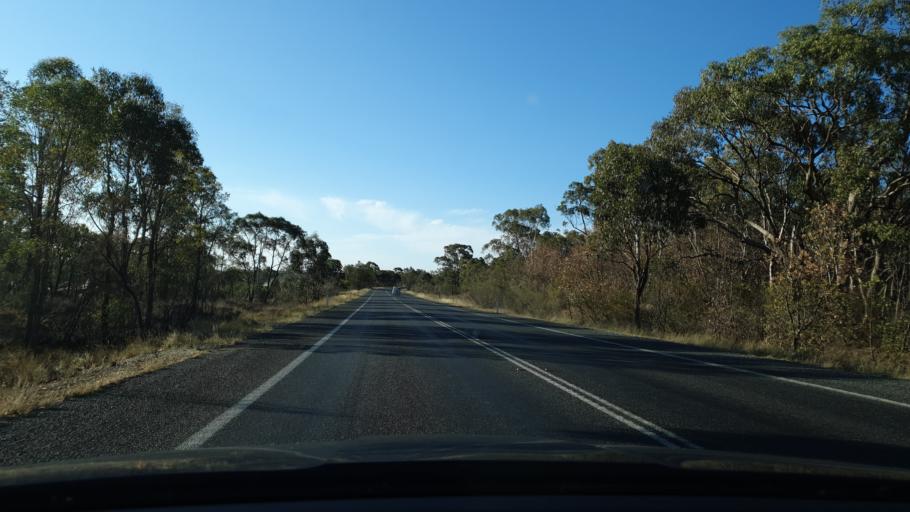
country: AU
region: Queensland
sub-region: Southern Downs
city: Stanthorpe
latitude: -28.6722
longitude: 151.9189
